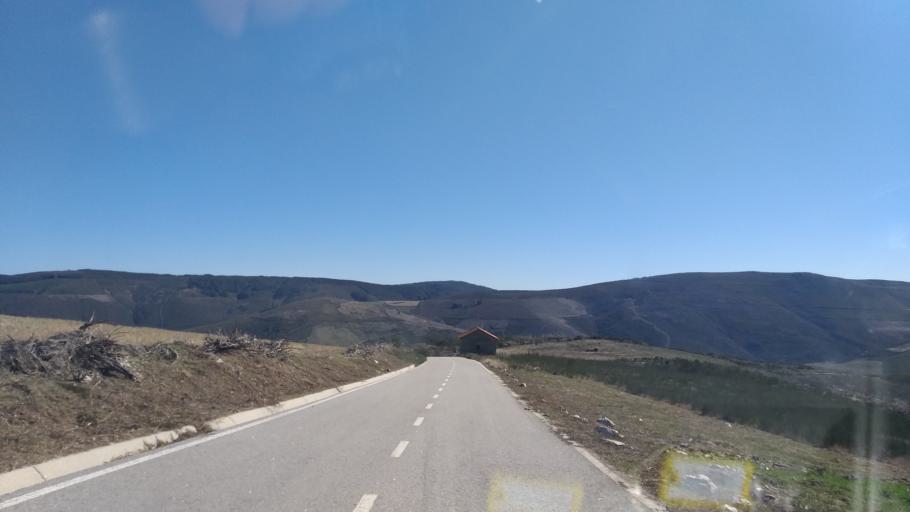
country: PT
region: Guarda
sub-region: Manteigas
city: Manteigas
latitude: 40.4712
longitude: -7.5048
